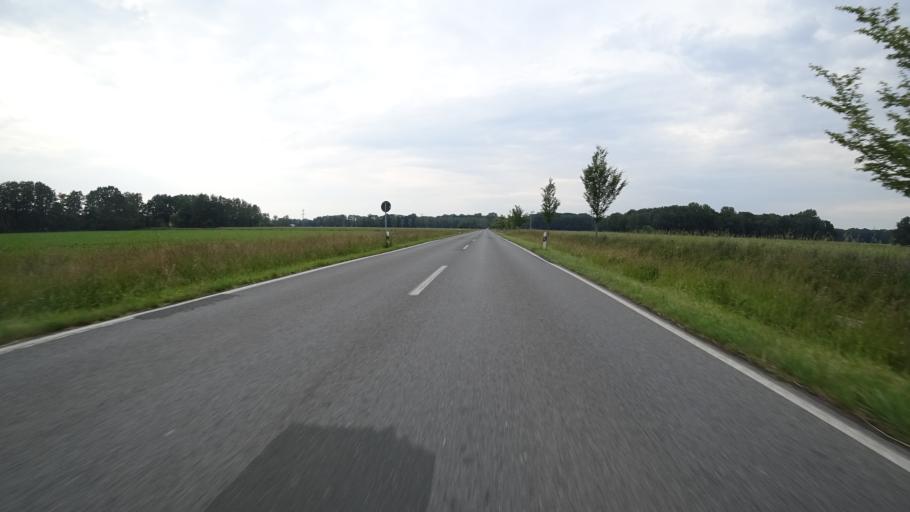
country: DE
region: North Rhine-Westphalia
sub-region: Regierungsbezirk Detmold
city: Guetersloh
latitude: 51.9362
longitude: 8.3799
